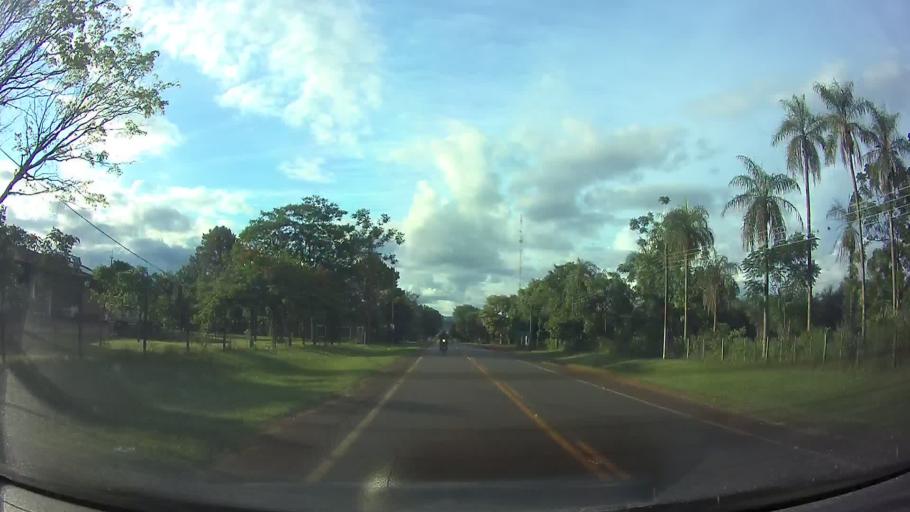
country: PY
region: Paraguari
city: Ybycui
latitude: -26.0114
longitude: -57.0352
